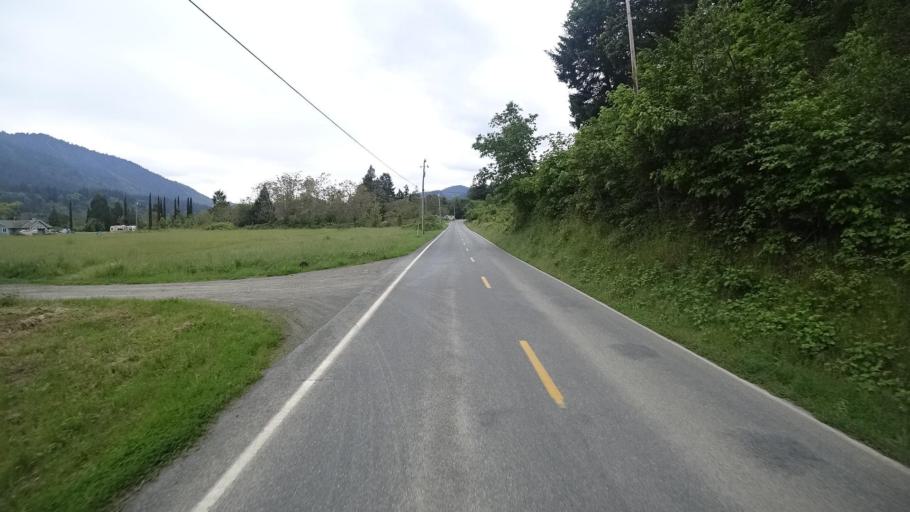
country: US
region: California
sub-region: Humboldt County
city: Willow Creek
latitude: 41.0745
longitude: -123.6946
